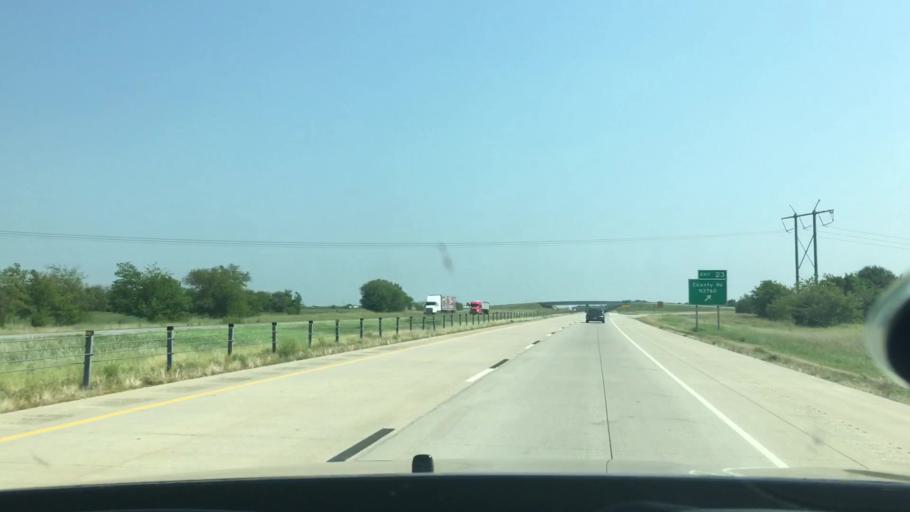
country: US
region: Oklahoma
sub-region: Bryan County
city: Durant
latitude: 34.0892
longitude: -96.3267
